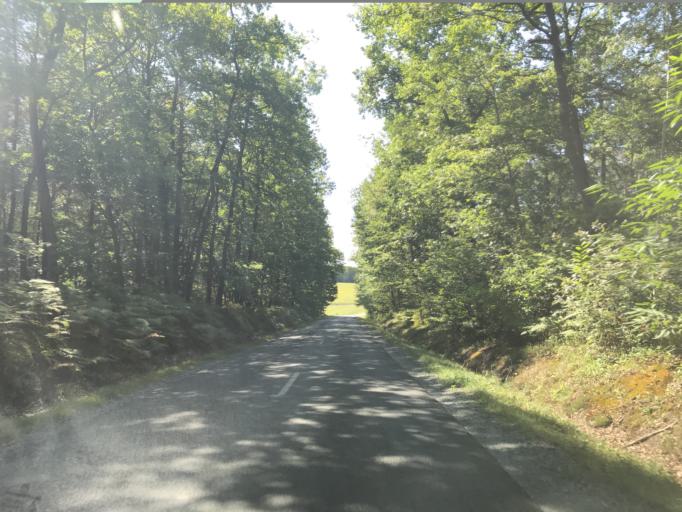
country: FR
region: Haute-Normandie
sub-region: Departement de l'Eure
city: Houlbec-Cocherel
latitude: 49.0845
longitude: 1.3233
